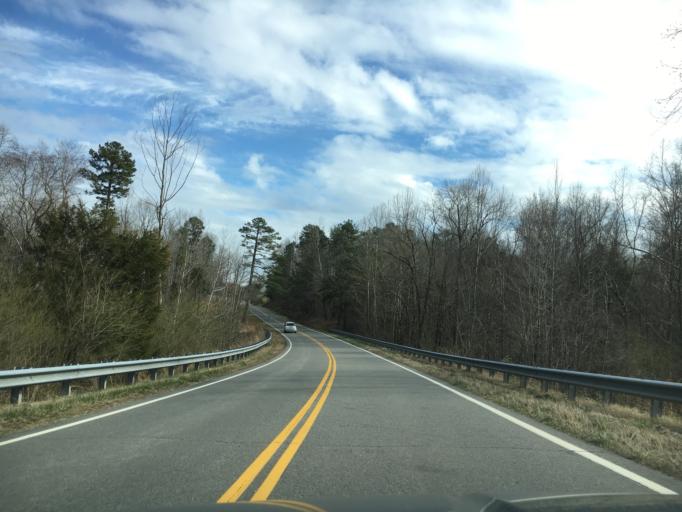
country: US
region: Virginia
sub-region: Halifax County
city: Halifax
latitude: 36.7639
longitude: -78.9153
